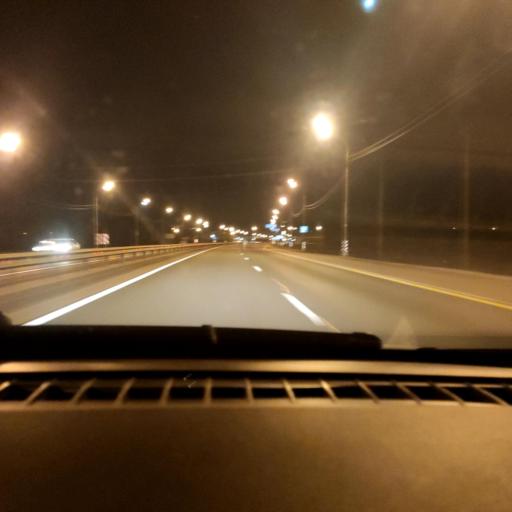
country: RU
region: Lipetsk
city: Khlevnoye
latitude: 52.2180
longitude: 39.1367
